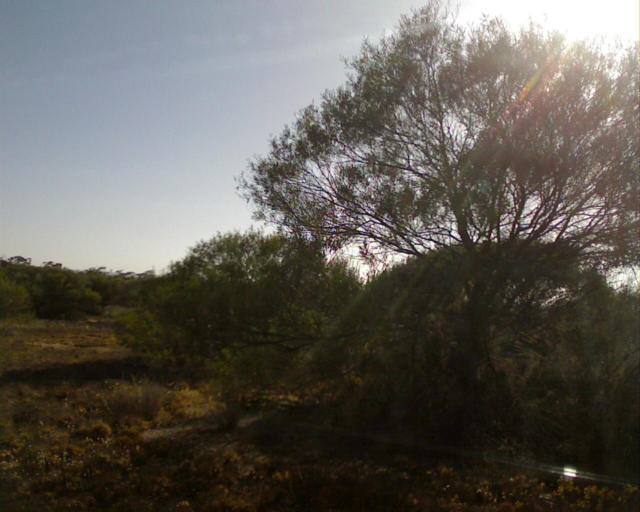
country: AU
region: Western Australia
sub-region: Wongan-Ballidu
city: Wongan Hills
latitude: -30.2902
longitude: 116.9658
